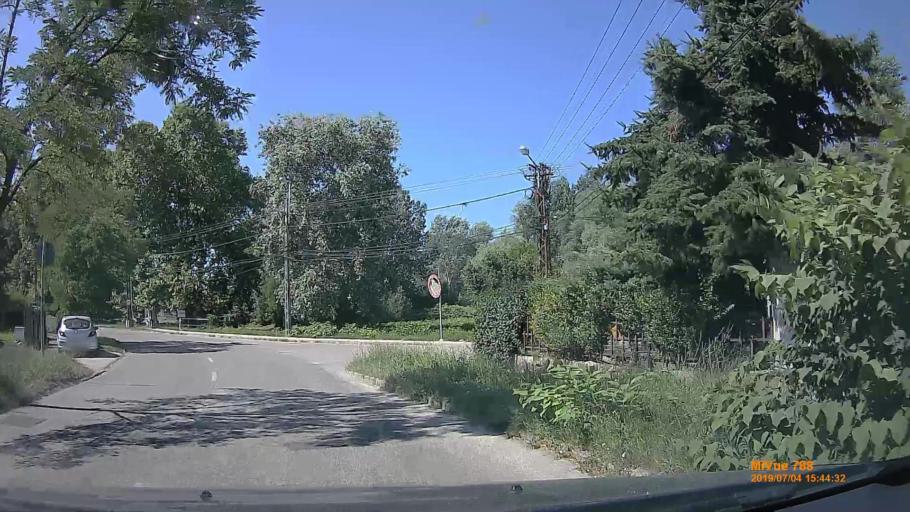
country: HU
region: Komarom-Esztergom
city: Tatabanya
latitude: 47.5678
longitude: 18.4171
